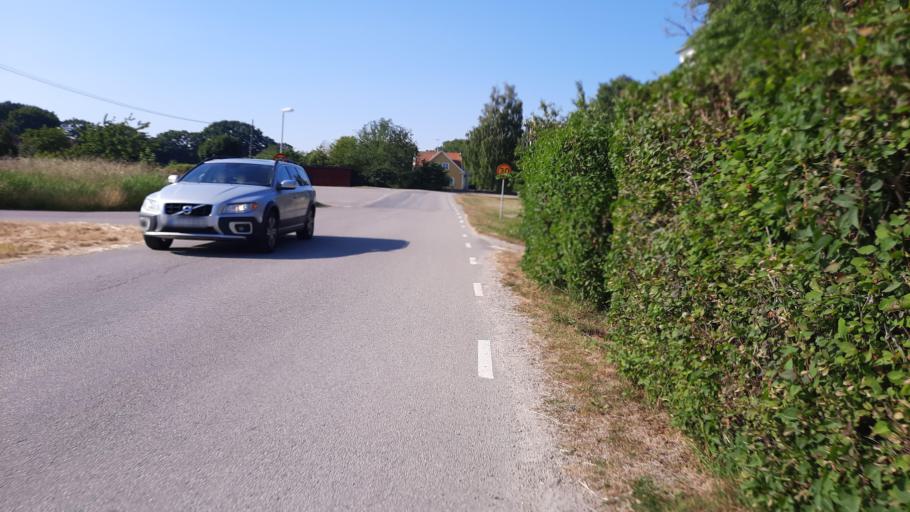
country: SE
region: Blekinge
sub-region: Karlskrona Kommun
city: Sturko
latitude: 56.0878
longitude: 15.6953
